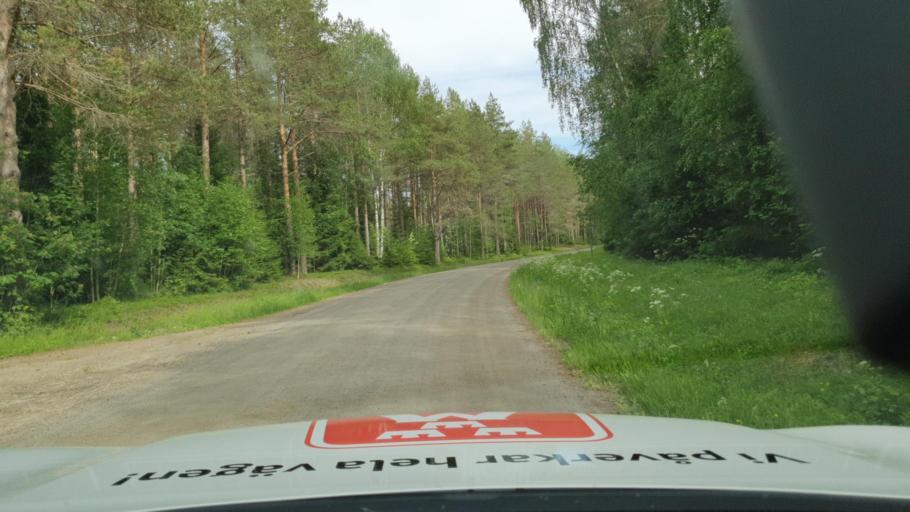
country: SE
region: Vaesterbotten
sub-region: Skelleftea Kommun
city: Burea
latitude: 64.3740
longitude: 21.0653
